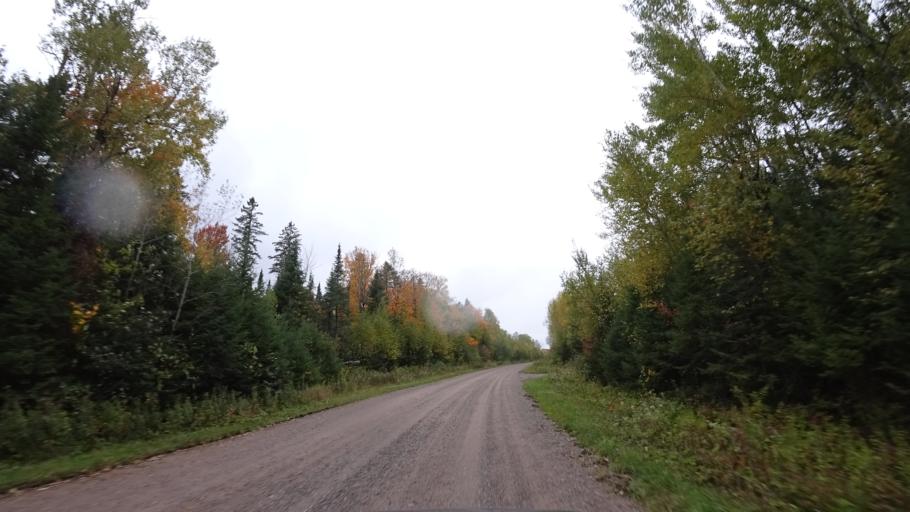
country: US
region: Wisconsin
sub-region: Sawyer County
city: Little Round Lake
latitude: 45.9786
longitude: -90.9952
